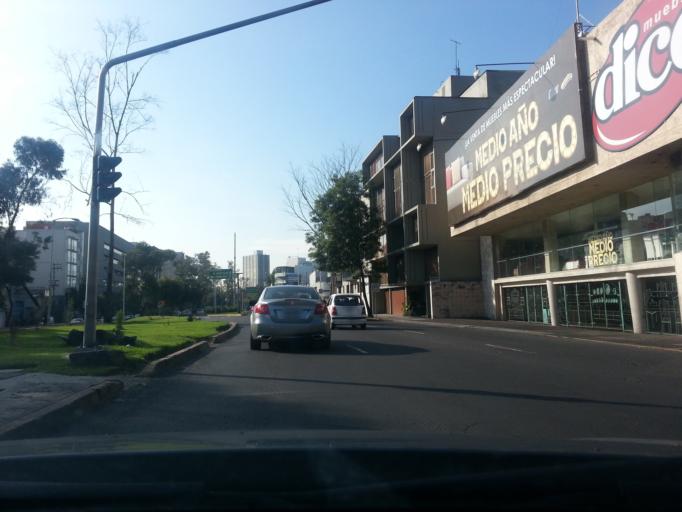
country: MX
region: Mexico City
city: Coyoacan
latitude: 19.3650
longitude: -99.1778
